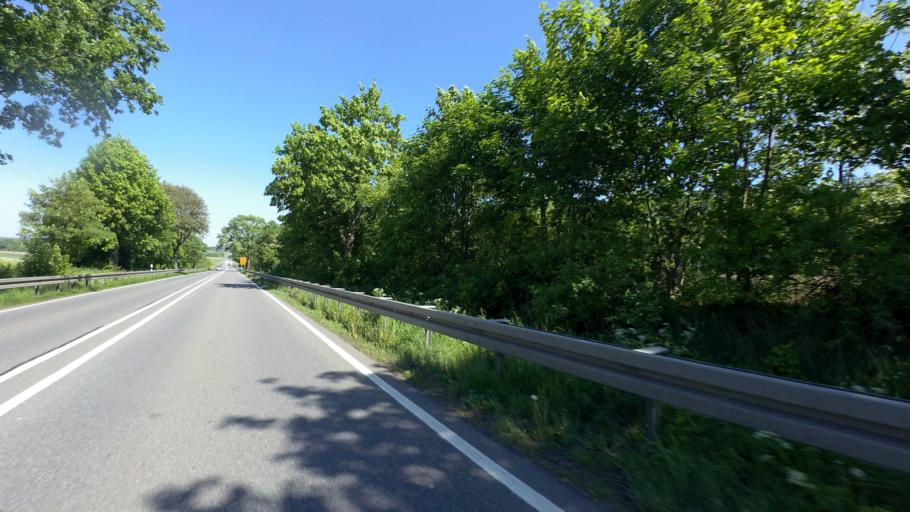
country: DE
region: Brandenburg
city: Spremberg
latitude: 51.6549
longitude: 14.3610
